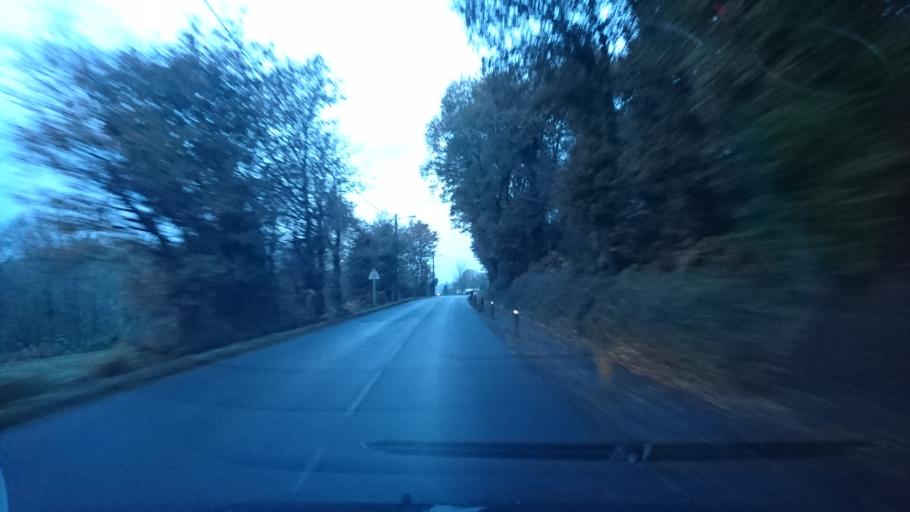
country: FR
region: Brittany
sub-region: Departement du Finistere
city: Chateaulin
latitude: 48.1908
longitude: -4.0840
